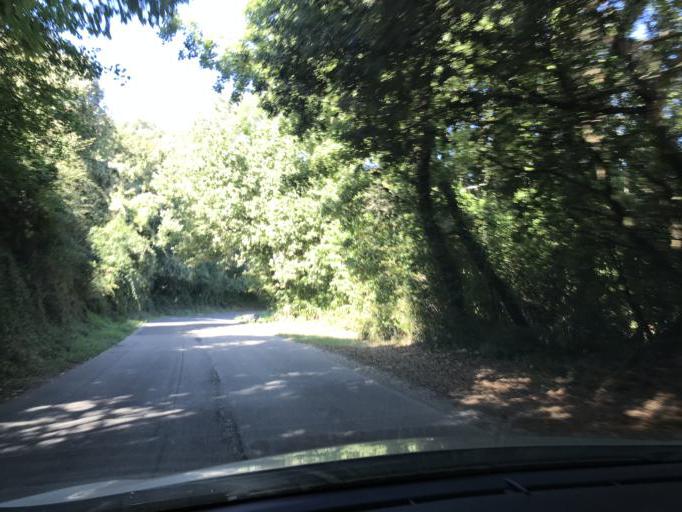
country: IT
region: Umbria
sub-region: Provincia di Terni
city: Avigliano Umbro
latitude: 42.6168
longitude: 12.4089
